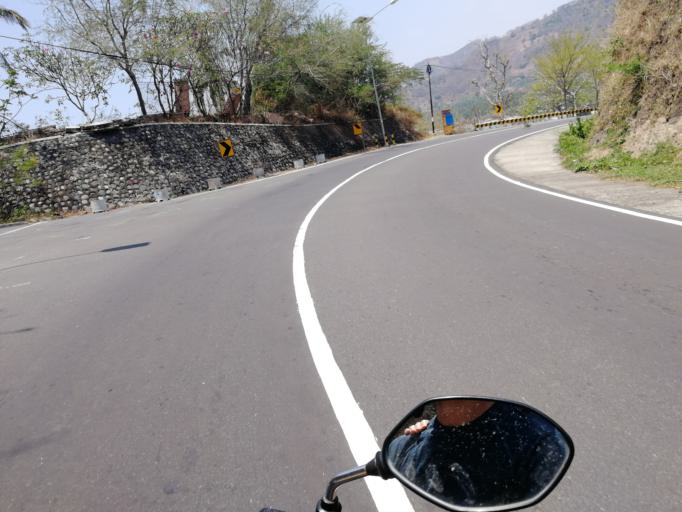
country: ID
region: West Nusa Tenggara
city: Karangsubagan
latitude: -8.4368
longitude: 116.0396
